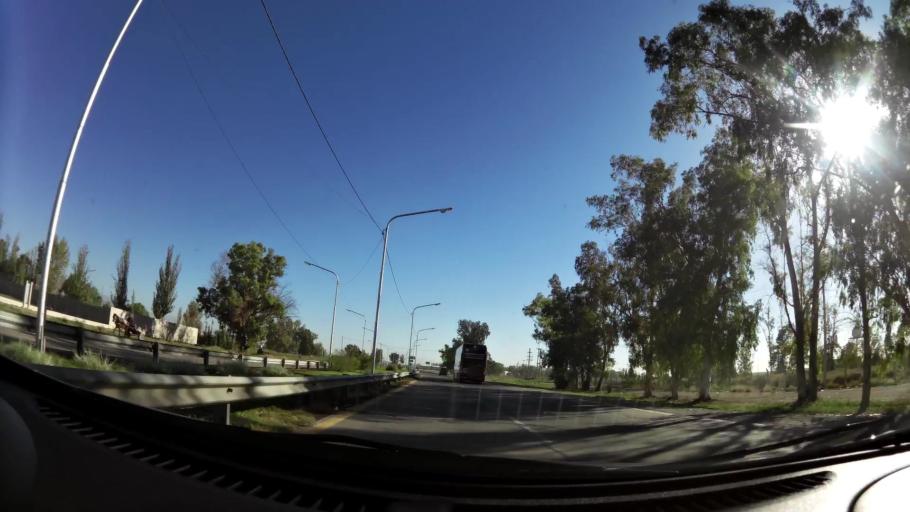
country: AR
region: Mendoza
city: Las Heras
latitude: -32.8250
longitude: -68.8035
